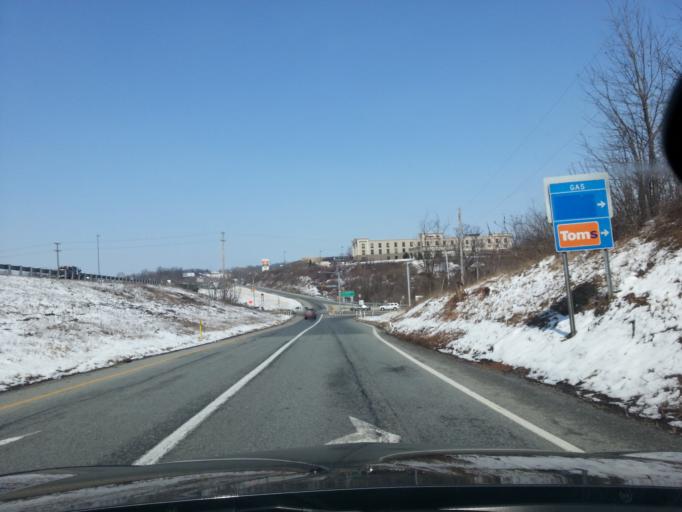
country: US
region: Pennsylvania
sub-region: York County
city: Shrewsbury
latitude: 39.7699
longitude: -76.6668
